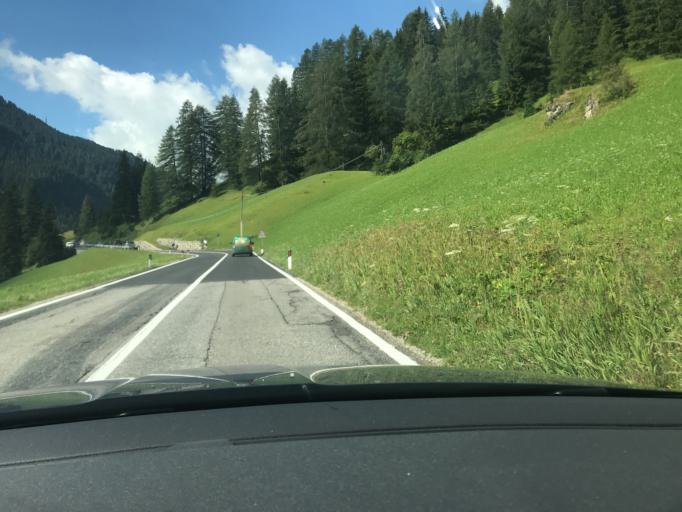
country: IT
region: Trentino-Alto Adige
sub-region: Bolzano
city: Corvara in Badia
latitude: 46.5730
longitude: 11.8916
